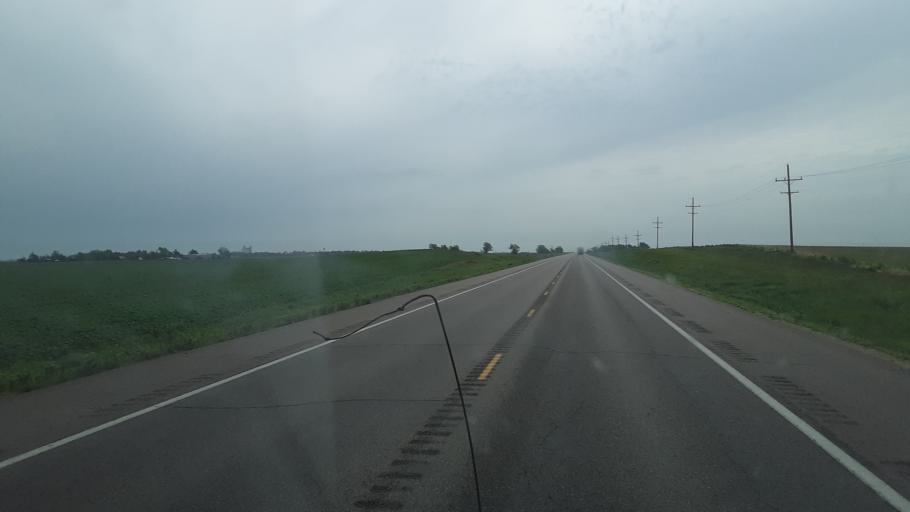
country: US
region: Kansas
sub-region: Edwards County
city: Kinsley
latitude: 37.9271
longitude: -99.2877
